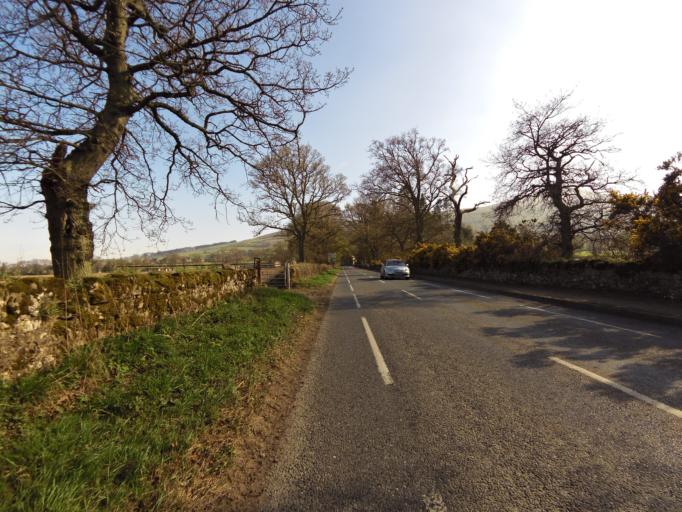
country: GB
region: Scotland
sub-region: Fife
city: Falkland
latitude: 56.2580
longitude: -3.2063
